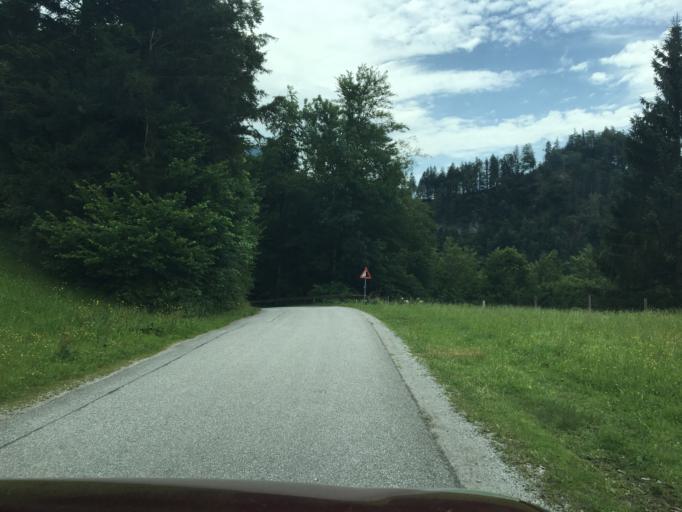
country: AT
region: Salzburg
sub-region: Politischer Bezirk Hallein
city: Scheffau am Tennengebirge
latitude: 47.6192
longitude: 13.1997
